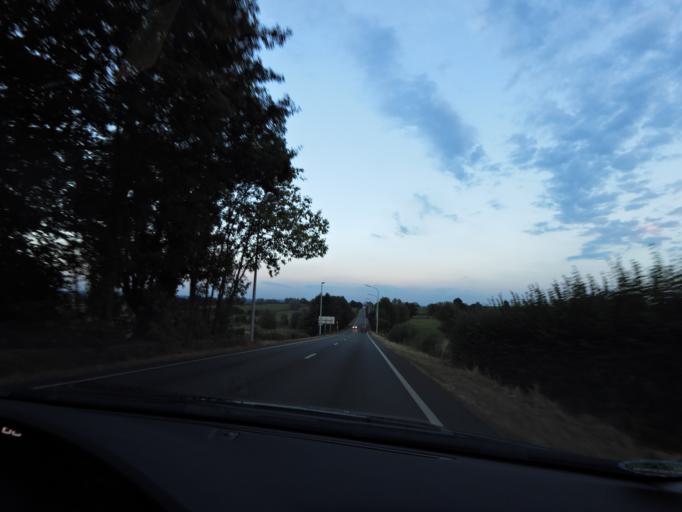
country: BE
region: Wallonia
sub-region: Province de Liege
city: Welkenraedt
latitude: 50.6837
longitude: 5.9556
